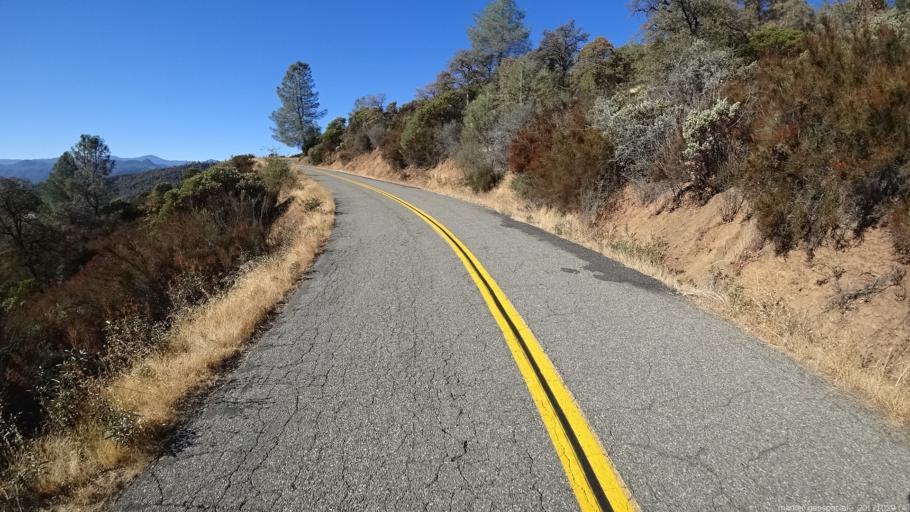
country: US
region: California
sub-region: Trinity County
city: Lewiston
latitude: 40.3854
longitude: -122.8373
